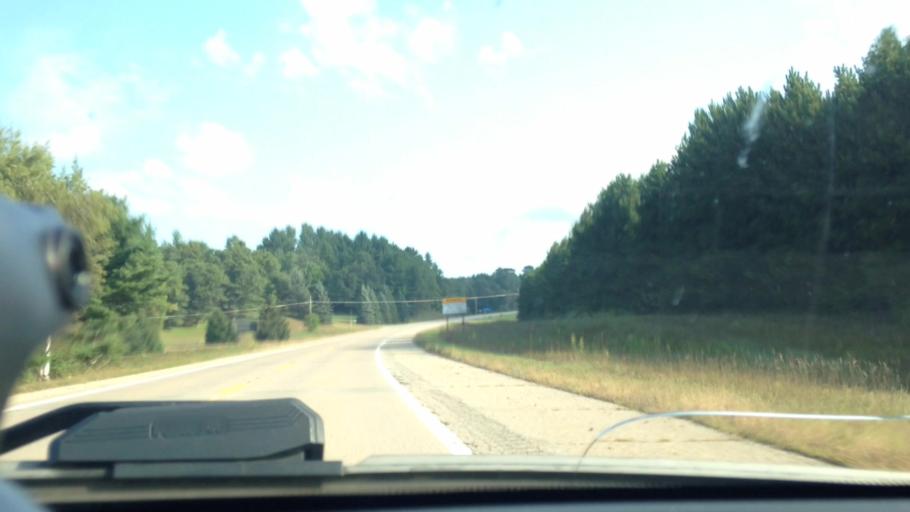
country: US
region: Michigan
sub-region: Dickinson County
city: Norway
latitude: 45.7598
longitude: -87.9214
